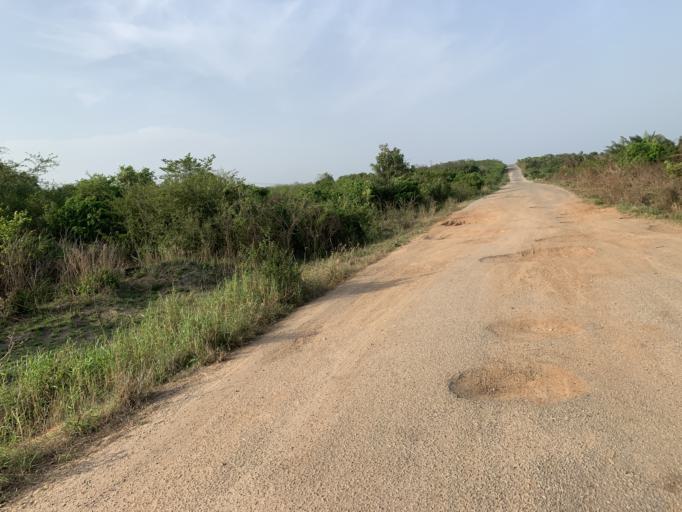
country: GH
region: Central
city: Winneba
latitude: 5.3832
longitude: -0.6071
